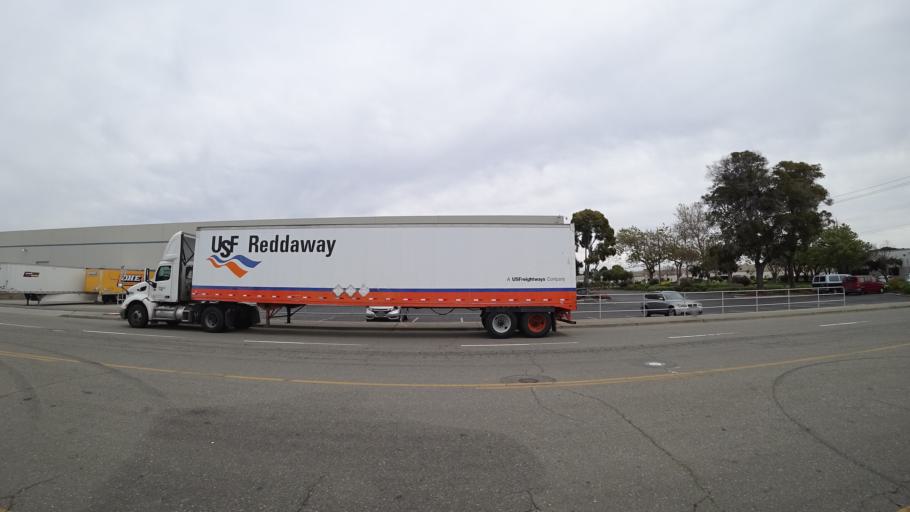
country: US
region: California
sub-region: Alameda County
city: San Lorenzo
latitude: 37.6533
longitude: -122.1388
